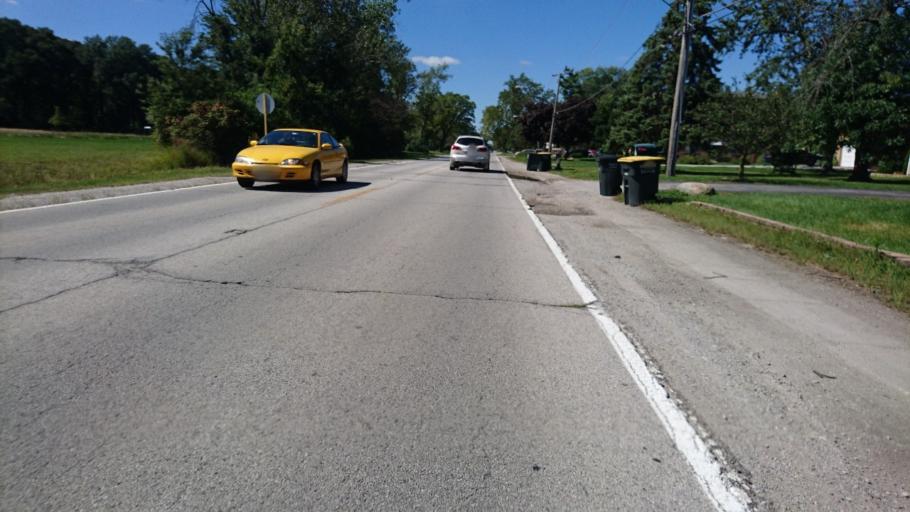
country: US
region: Illinois
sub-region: Cook County
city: Lansing
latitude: 41.5575
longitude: -87.5494
